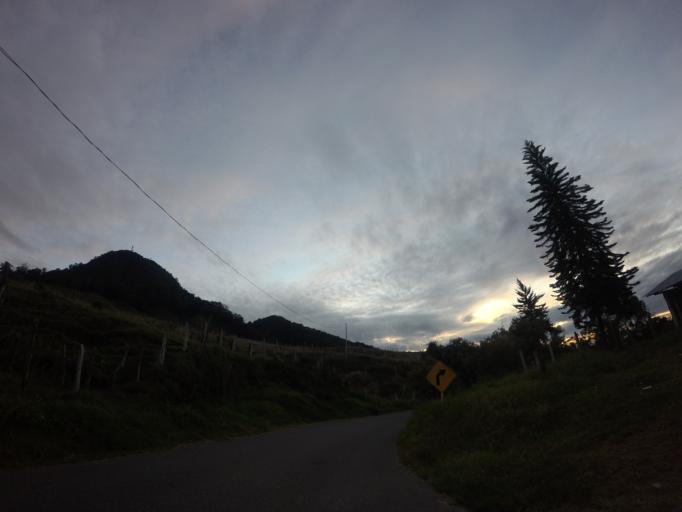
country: CO
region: Caldas
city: Manzanares
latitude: 5.2716
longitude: -75.1367
